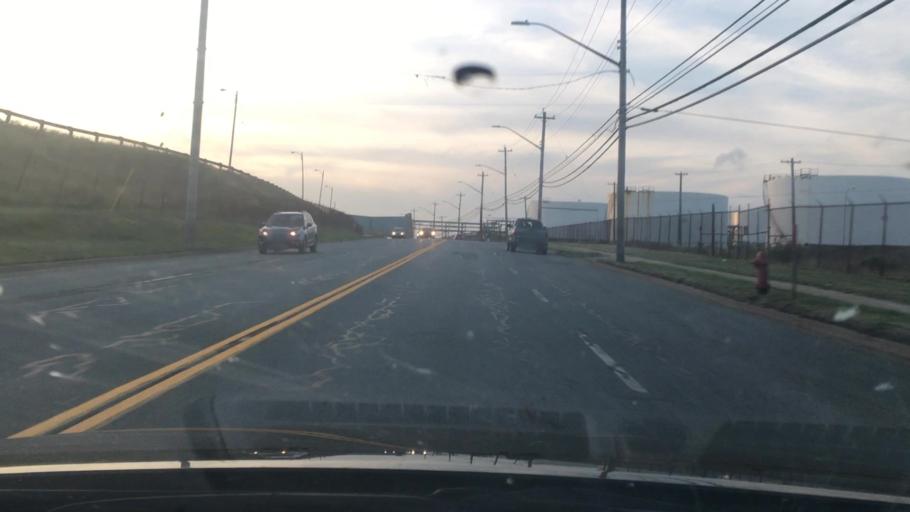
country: CA
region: Nova Scotia
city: Halifax
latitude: 44.6390
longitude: -63.5309
